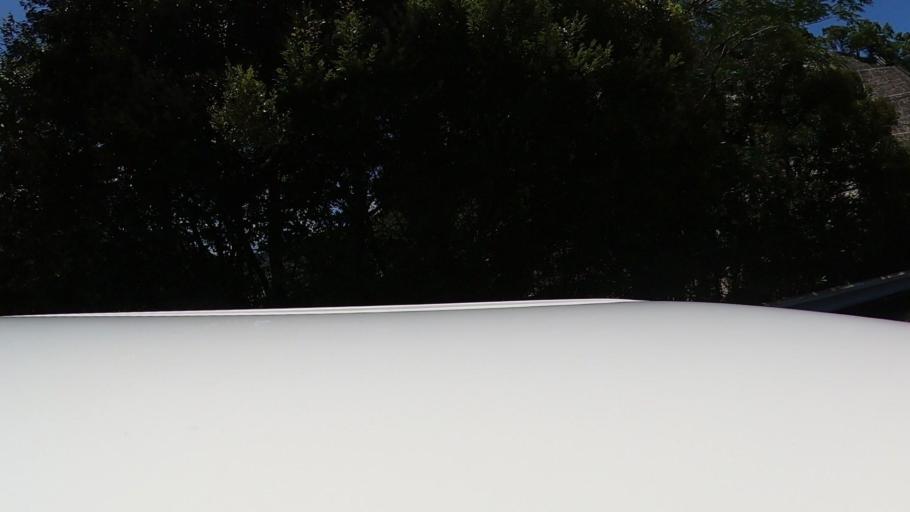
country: JP
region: Miyazaki
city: Nobeoka
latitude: 32.5240
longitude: 131.6652
